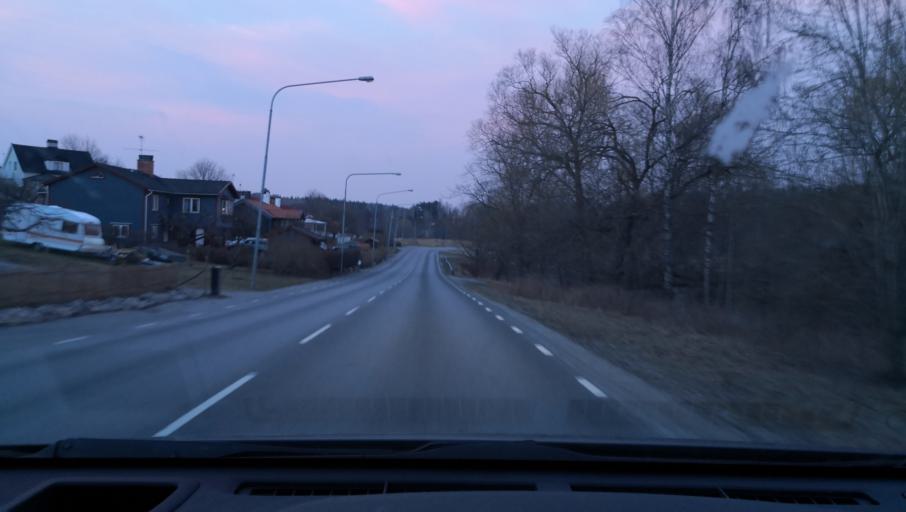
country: SE
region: OErebro
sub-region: Lindesbergs Kommun
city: Lindesberg
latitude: 59.5893
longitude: 15.2420
